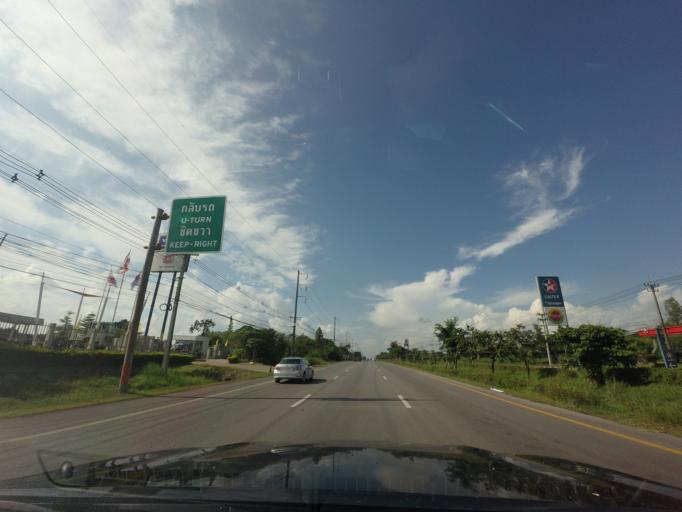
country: TH
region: Nong Khai
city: Nong Khai
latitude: 17.8015
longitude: 102.7613
